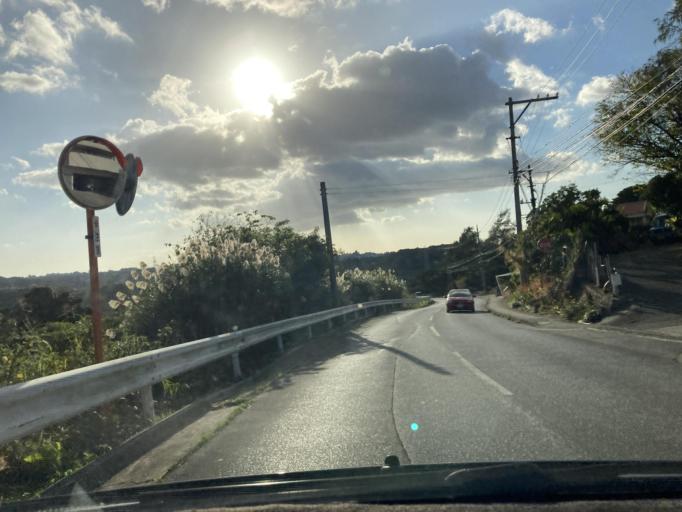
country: JP
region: Okinawa
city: Chatan
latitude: 26.2914
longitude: 127.7941
